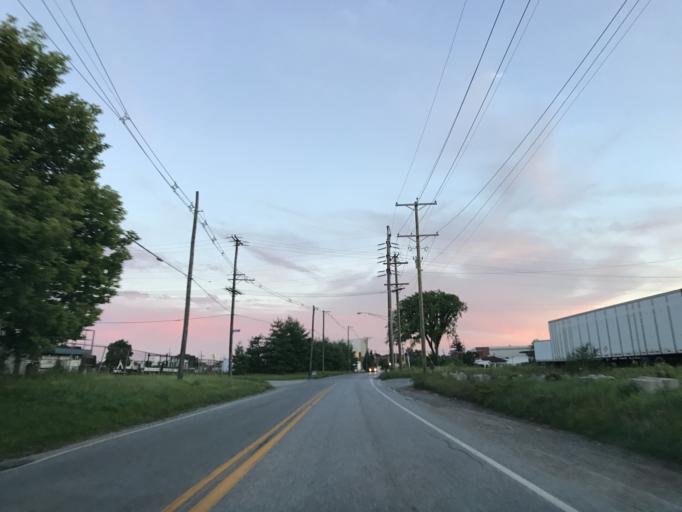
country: US
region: Pennsylvania
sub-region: York County
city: North York
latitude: 39.9768
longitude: -76.7231
